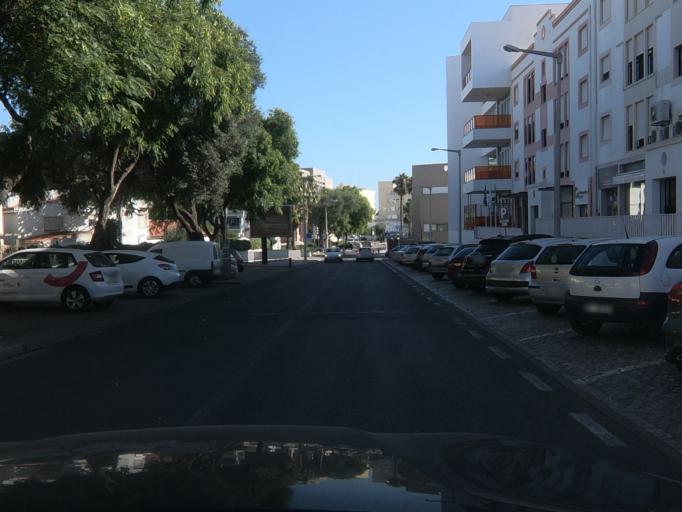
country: PT
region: Faro
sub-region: Loule
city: Loule
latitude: 37.1398
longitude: -8.0180
